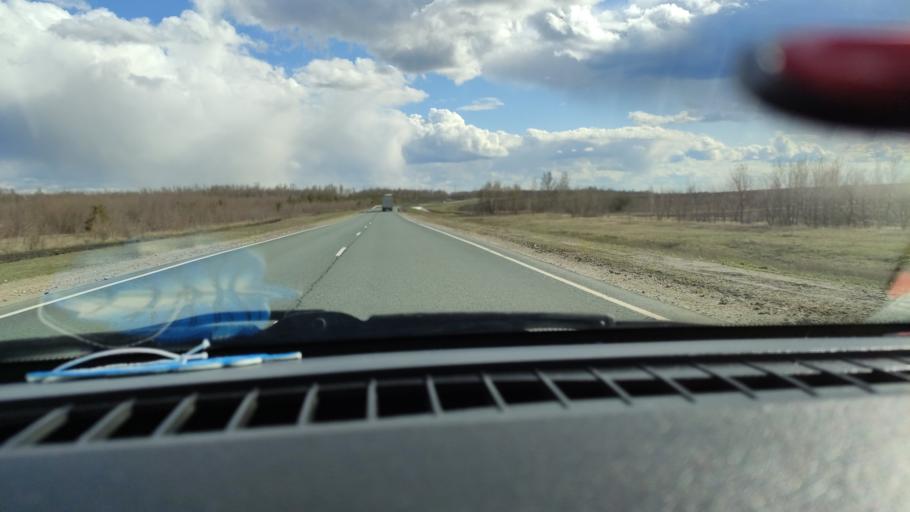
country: RU
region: Saratov
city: Alekseyevka
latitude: 52.2789
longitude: 47.9316
